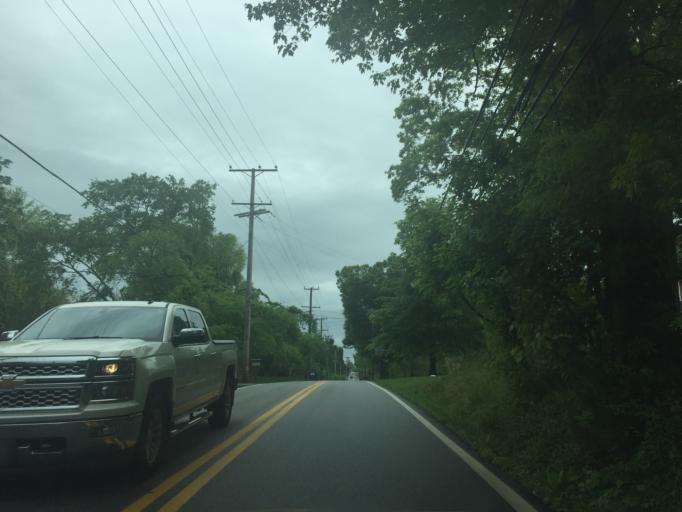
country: US
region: Maryland
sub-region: Baltimore County
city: Perry Hall
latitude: 39.4073
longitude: -76.4556
